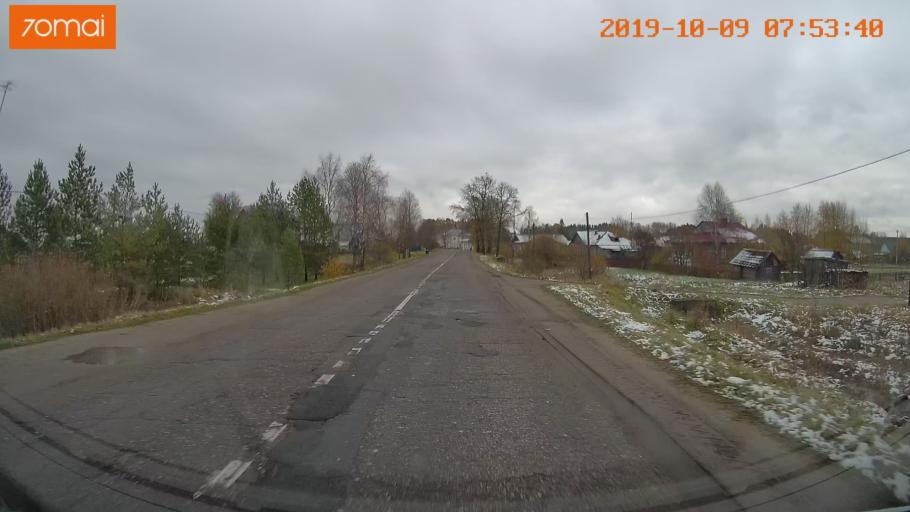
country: RU
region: Jaroslavl
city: Kukoboy
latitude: 58.6982
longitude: 39.8978
